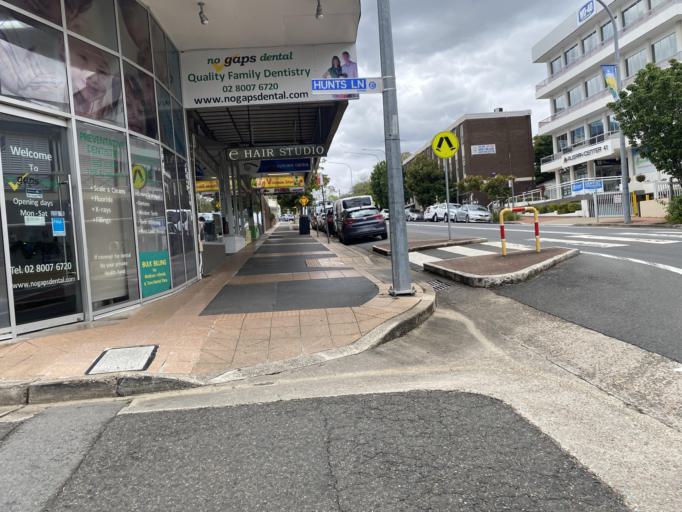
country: AU
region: New South Wales
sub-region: Parramatta
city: Epping
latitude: -33.7734
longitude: 151.0809
